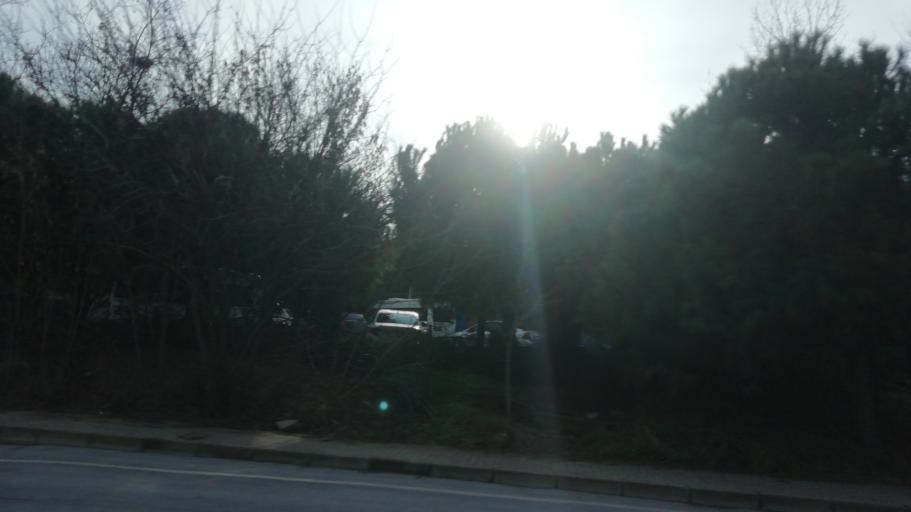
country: TR
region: Istanbul
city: Basaksehir
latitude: 41.0849
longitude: 28.8077
